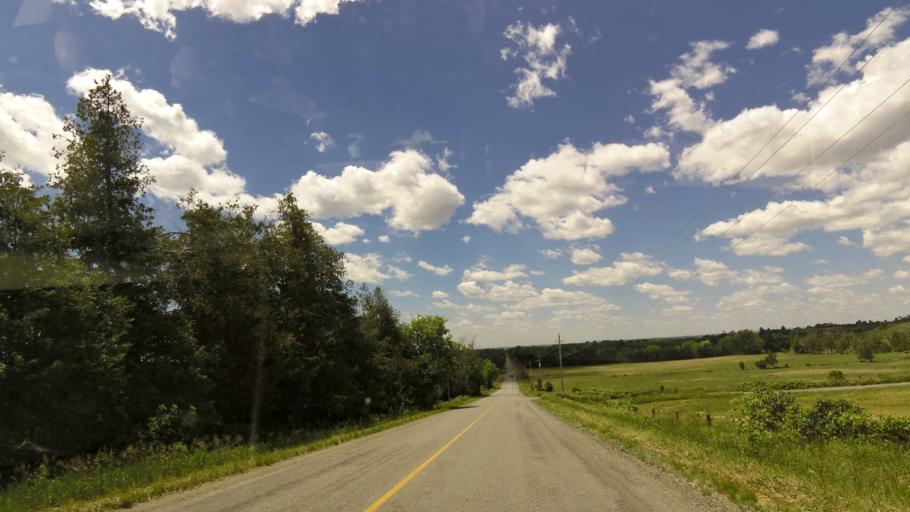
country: CA
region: Ontario
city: Oshawa
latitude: 43.9620
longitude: -78.5638
